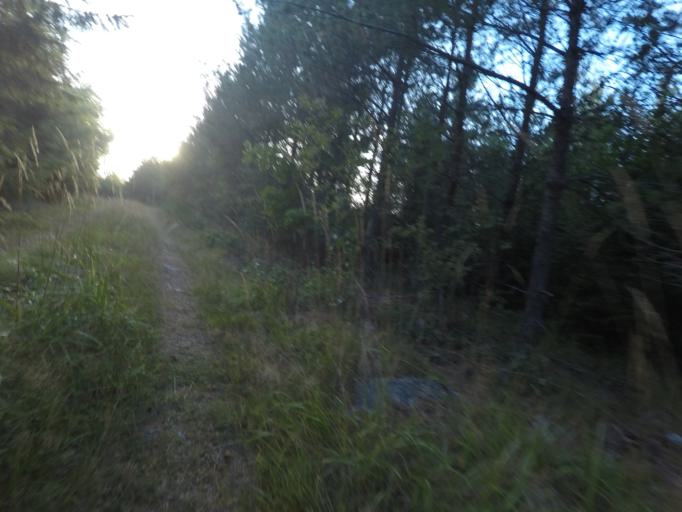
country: SE
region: Soedermanland
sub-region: Eskilstuna Kommun
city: Kvicksund
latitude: 59.4204
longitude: 16.3162
